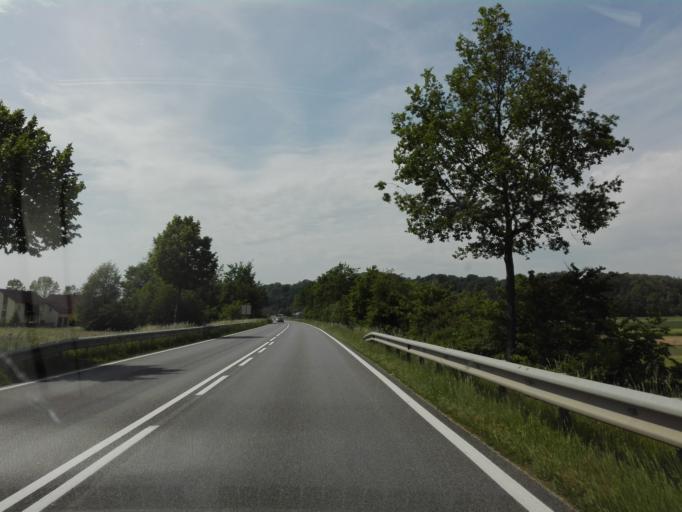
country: AT
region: Upper Austria
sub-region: Politischer Bezirk Perg
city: Bad Kreuzen
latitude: 48.2208
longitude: 14.7326
